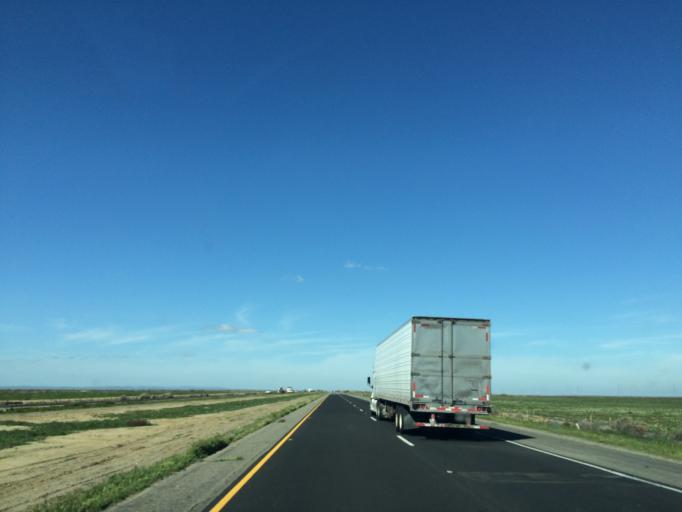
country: US
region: California
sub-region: Kern County
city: Lost Hills
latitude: 35.7697
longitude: -119.7674
